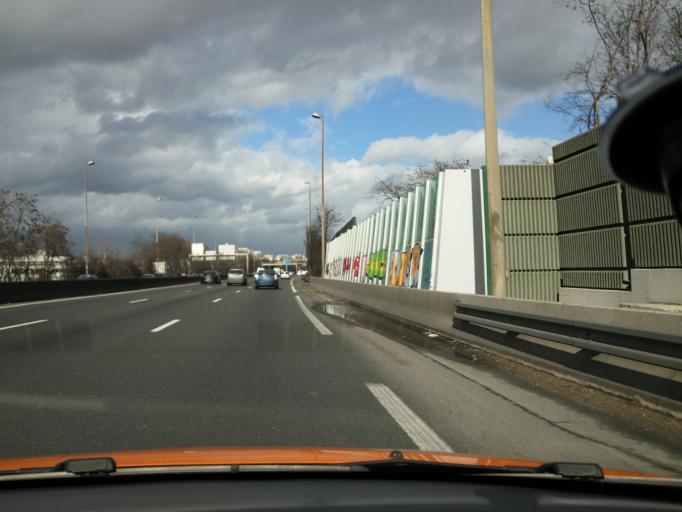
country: FR
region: Ile-de-France
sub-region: Departement du Val-de-Marne
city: Maisons-Alfort
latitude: 48.7877
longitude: 2.4404
